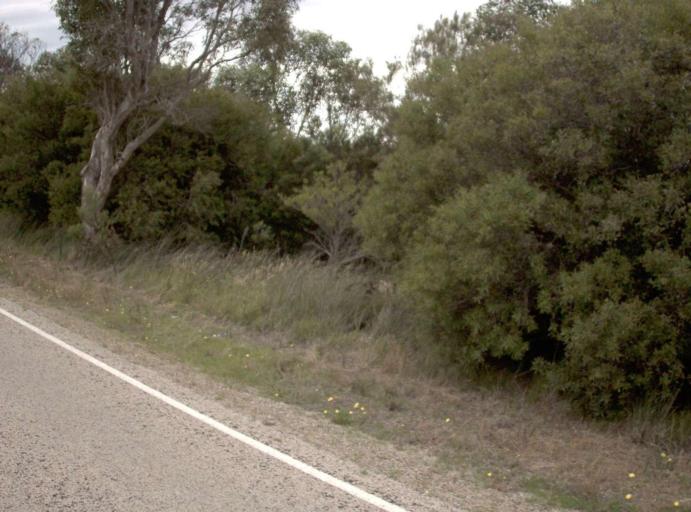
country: AU
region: Victoria
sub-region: East Gippsland
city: Bairnsdale
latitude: -37.9152
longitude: 147.5500
